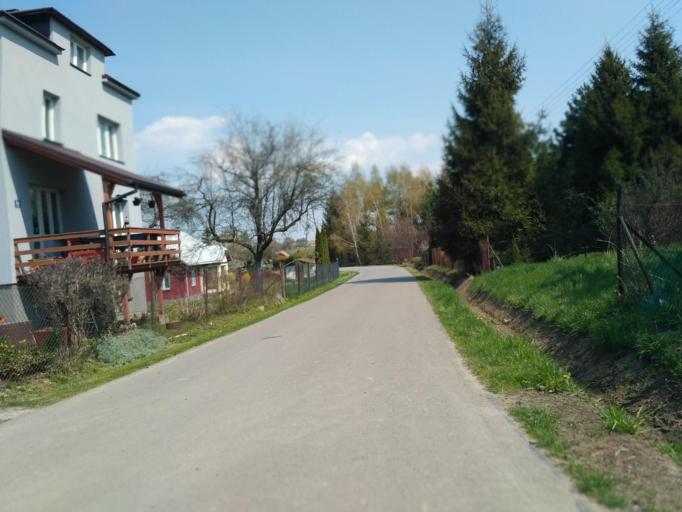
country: PL
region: Subcarpathian Voivodeship
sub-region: Powiat krosnienski
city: Chorkowka
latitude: 49.6261
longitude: 21.7037
